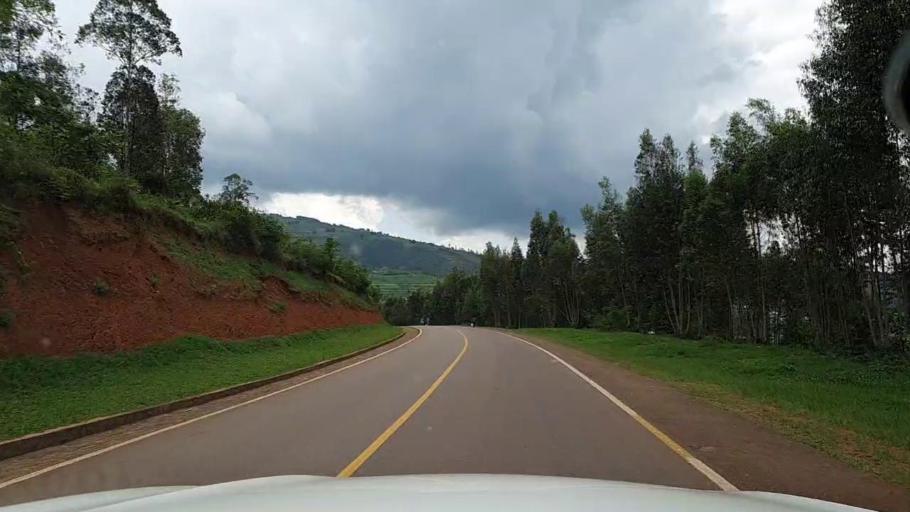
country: RW
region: Kigali
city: Kigali
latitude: -1.7745
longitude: 30.1268
